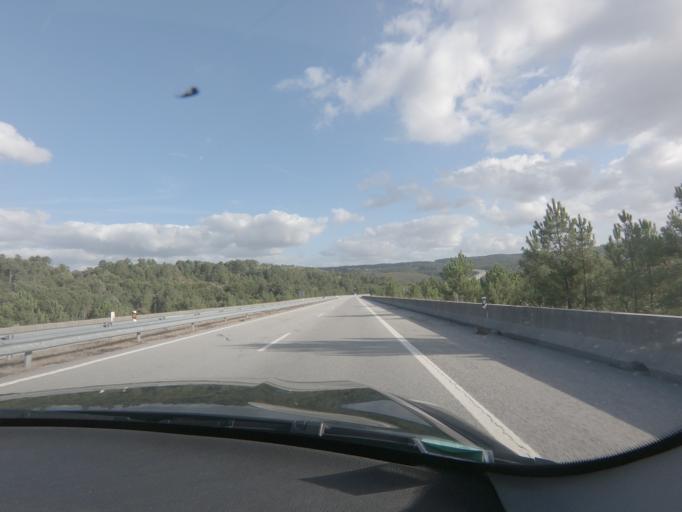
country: PT
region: Viseu
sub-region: Viseu
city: Campo
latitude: 40.7608
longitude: -7.9225
